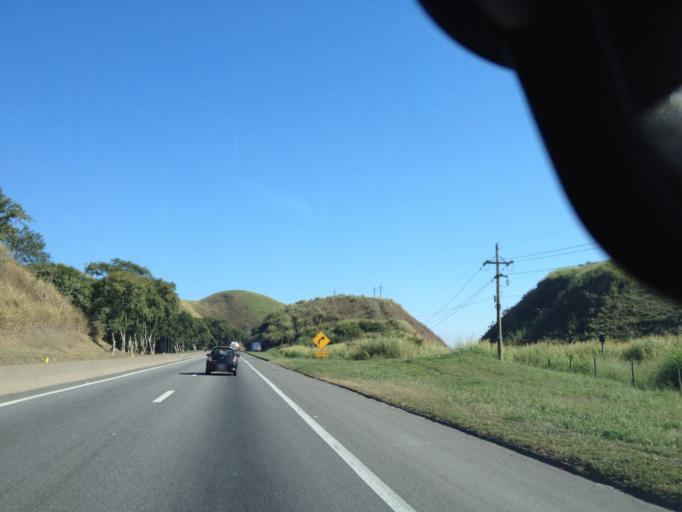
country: BR
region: Rio de Janeiro
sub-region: Porto Real
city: Porto Real
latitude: -22.4741
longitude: -44.2721
